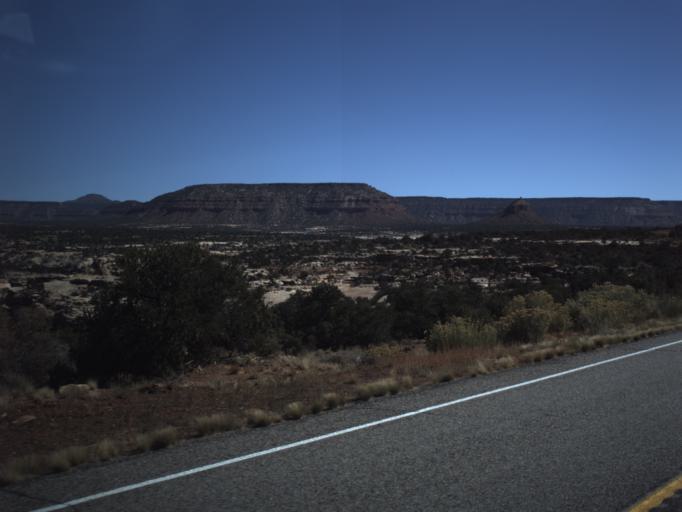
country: US
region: Utah
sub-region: San Juan County
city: Blanding
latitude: 37.6535
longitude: -110.1319
